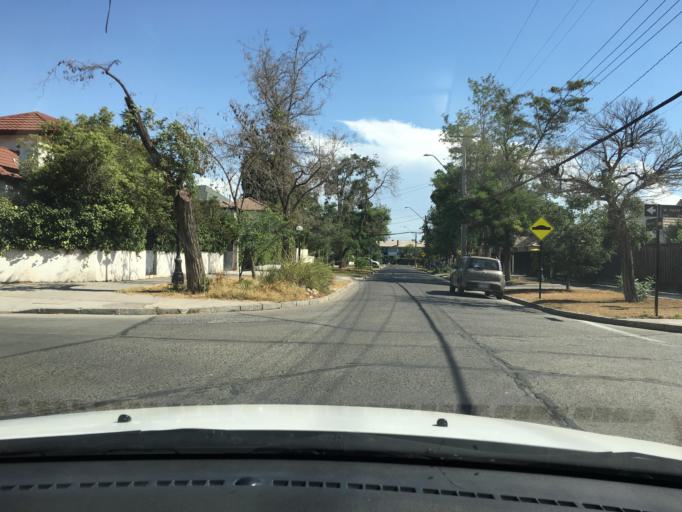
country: CL
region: Santiago Metropolitan
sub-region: Provincia de Santiago
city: Villa Presidente Frei, Nunoa, Santiago, Chile
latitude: -33.4428
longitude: -70.5910
